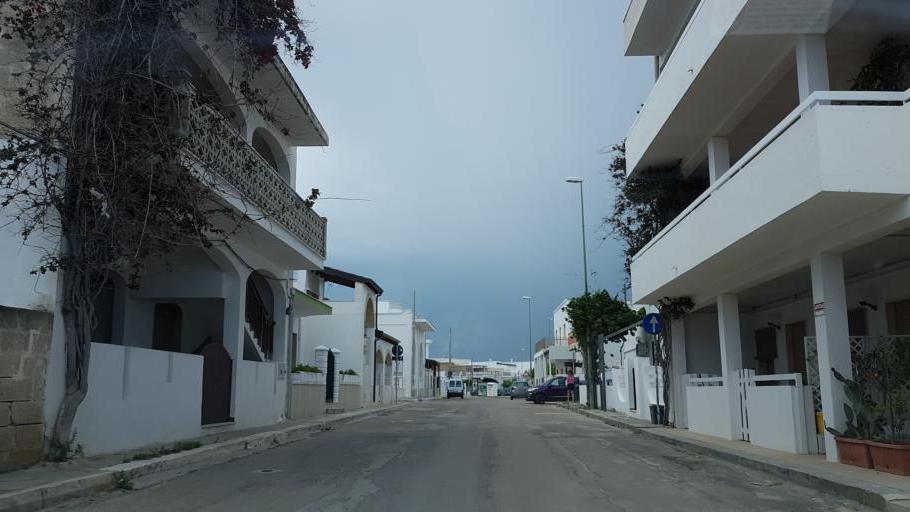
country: IT
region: Apulia
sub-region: Provincia di Lecce
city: Porto Cesareo
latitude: 40.2873
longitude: 17.8505
